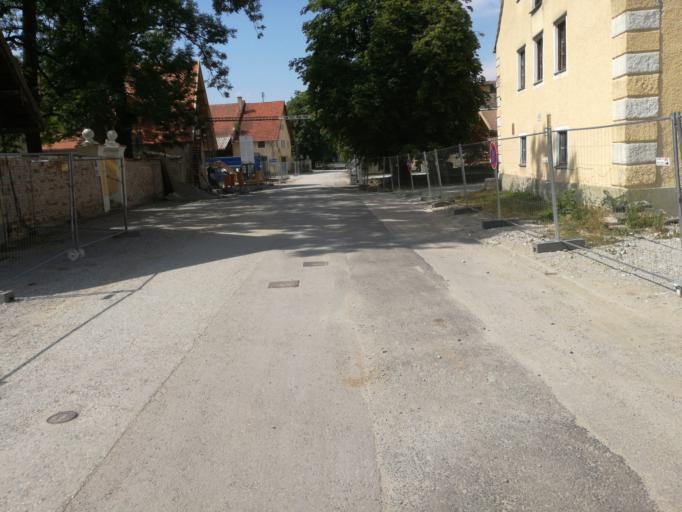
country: DE
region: Bavaria
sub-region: Upper Bavaria
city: Germering
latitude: 48.1369
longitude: 11.4023
